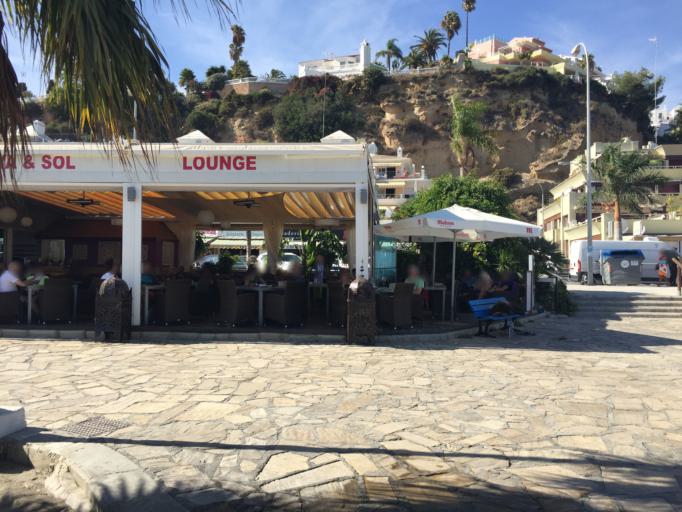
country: ES
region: Andalusia
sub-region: Provincia de Malaga
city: Nerja
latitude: 36.7507
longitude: -3.8669
